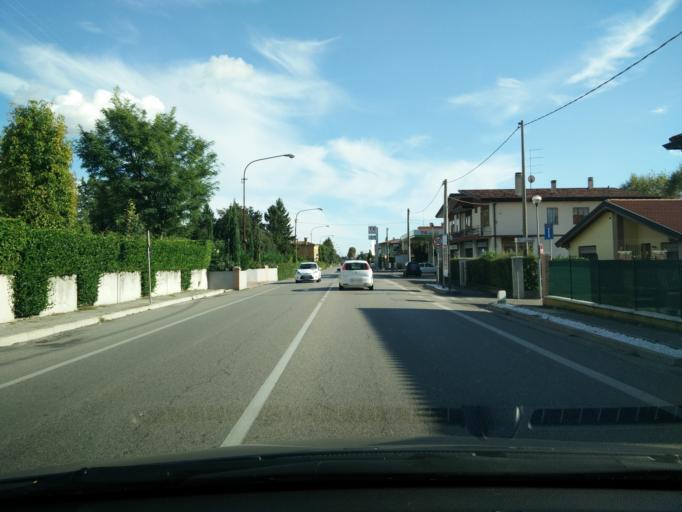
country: IT
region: Veneto
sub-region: Provincia di Venezia
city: Noventa di Piave
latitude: 45.6569
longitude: 12.5346
